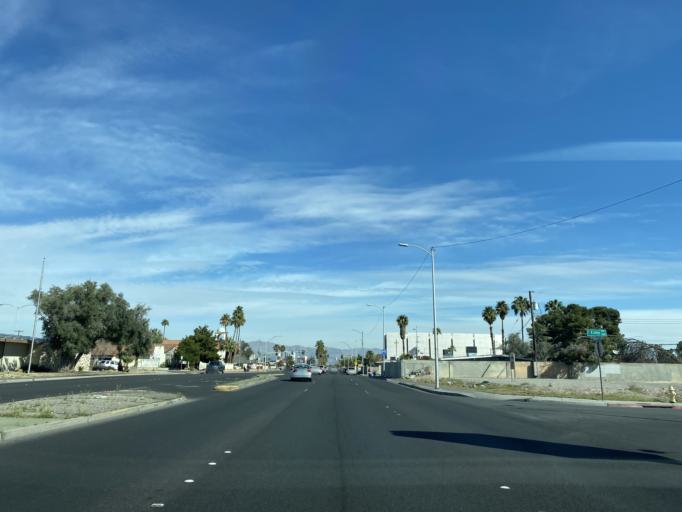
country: US
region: Nevada
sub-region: Clark County
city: Winchester
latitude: 36.1461
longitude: -115.1370
